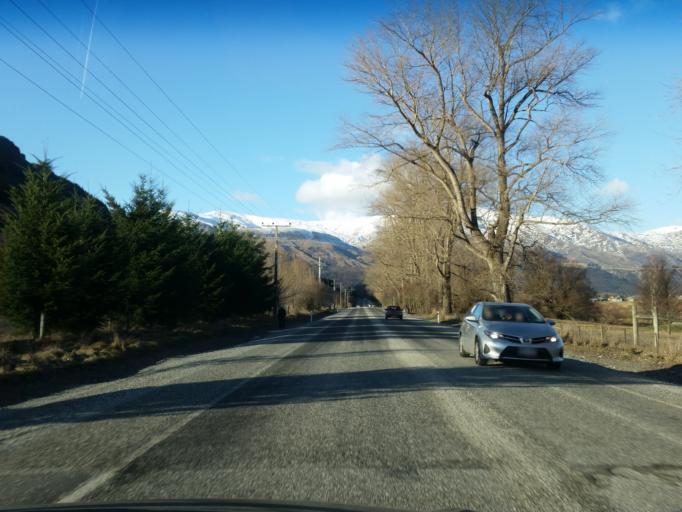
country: NZ
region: Otago
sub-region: Queenstown-Lakes District
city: Arrowtown
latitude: -44.9463
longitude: 168.7879
